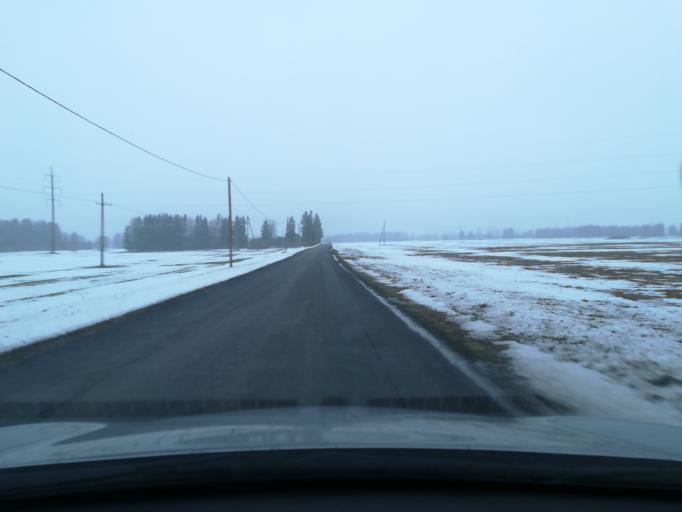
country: EE
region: Harju
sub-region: Raasiku vald
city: Raasiku
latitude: 59.3582
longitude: 25.1996
